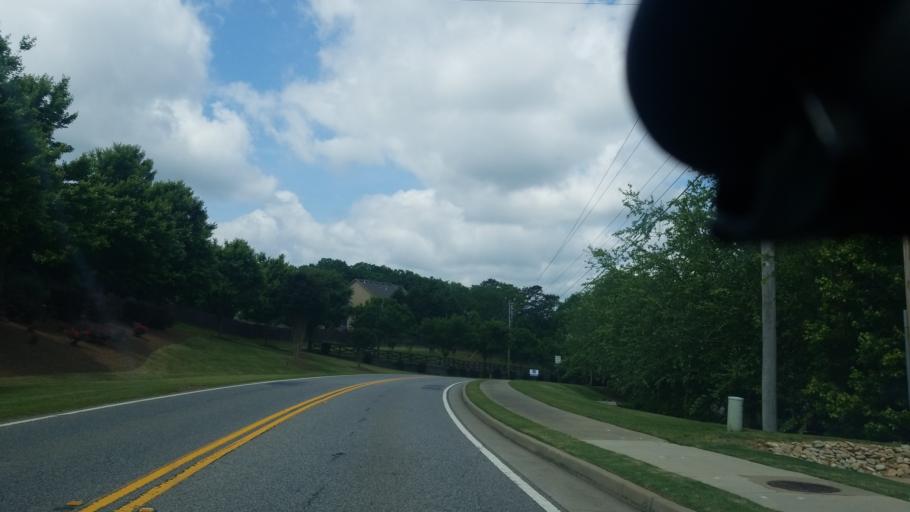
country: US
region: Georgia
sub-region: Forsyth County
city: Cumming
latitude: 34.1423
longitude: -84.1812
